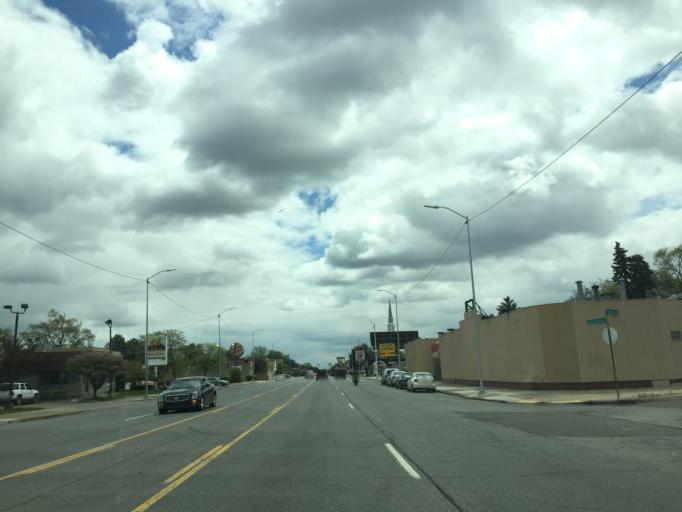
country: US
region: Michigan
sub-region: Wayne County
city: Redford
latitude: 42.4098
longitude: -83.2410
